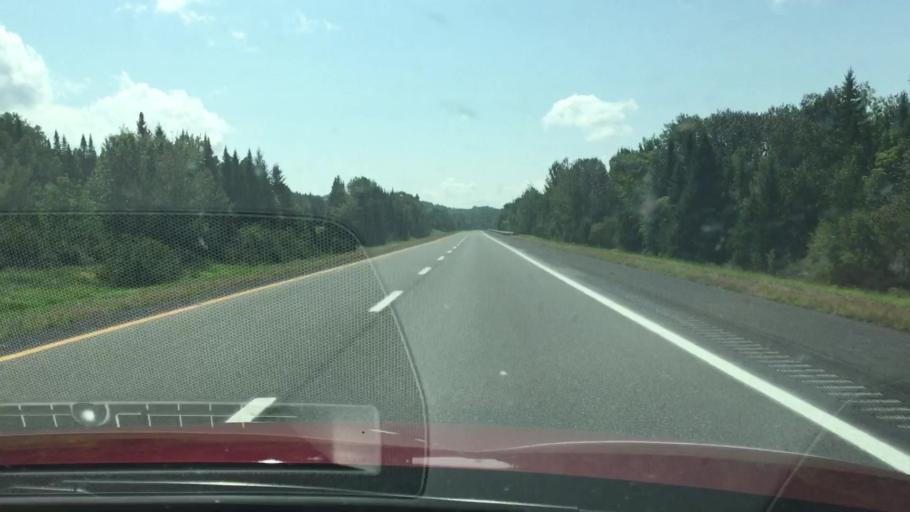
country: US
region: Maine
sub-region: Penobscot County
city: Patten
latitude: 45.9271
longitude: -68.3647
